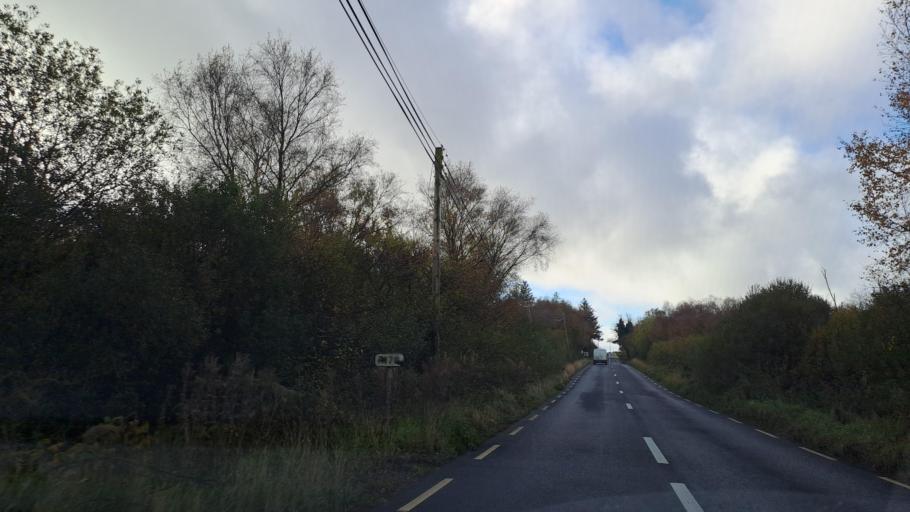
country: IE
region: Ulster
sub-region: An Cabhan
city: Virginia
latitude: 53.8501
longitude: -7.0596
